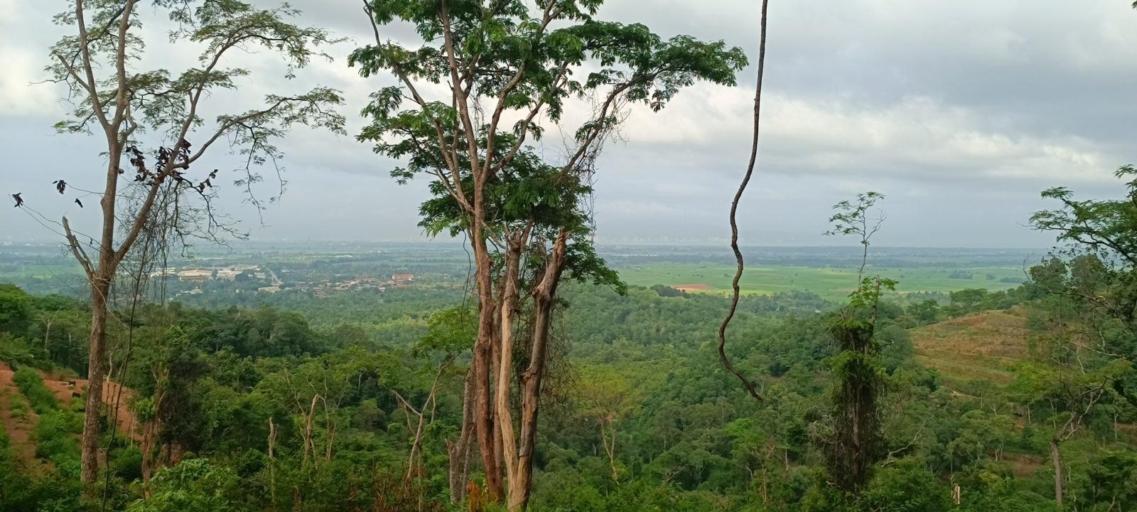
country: MY
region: Kedah
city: Sungai Petani
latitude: 5.6042
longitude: 100.4485
